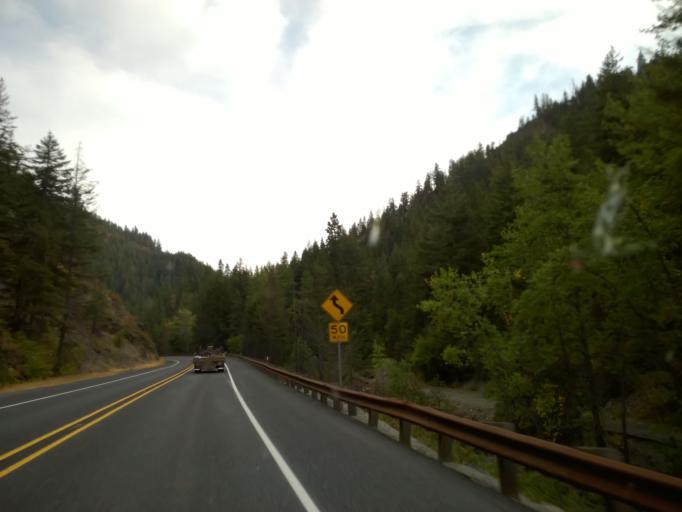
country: US
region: Washington
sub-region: Chelan County
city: Leavenworth
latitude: 47.4334
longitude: -120.6572
